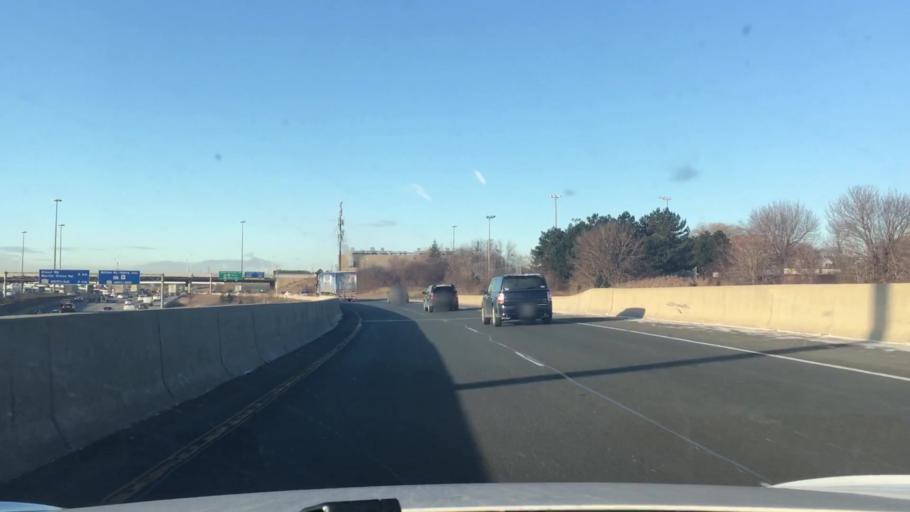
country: CA
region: Ontario
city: Etobicoke
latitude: 43.7115
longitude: -79.5472
